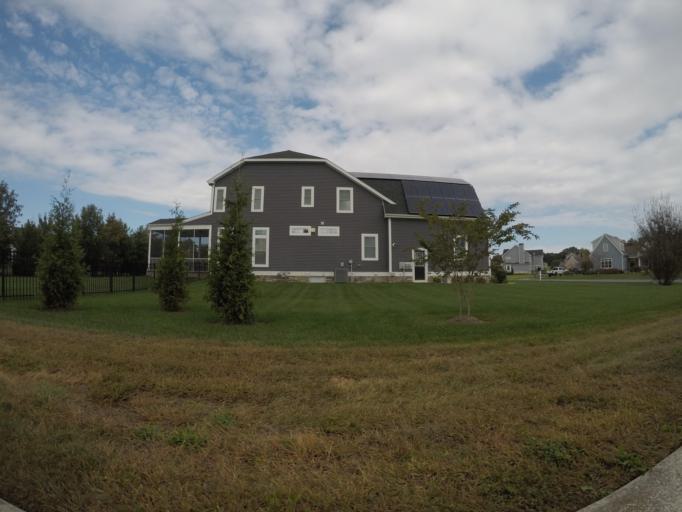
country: US
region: Delaware
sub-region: Sussex County
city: Lewes
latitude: 38.7531
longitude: -75.1332
